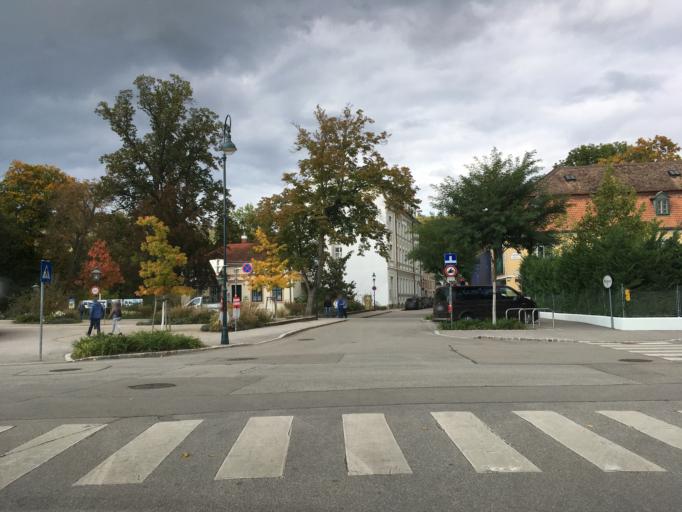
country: AT
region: Lower Austria
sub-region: Politischer Bezirk Baden
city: Baden
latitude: 48.0069
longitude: 16.2266
